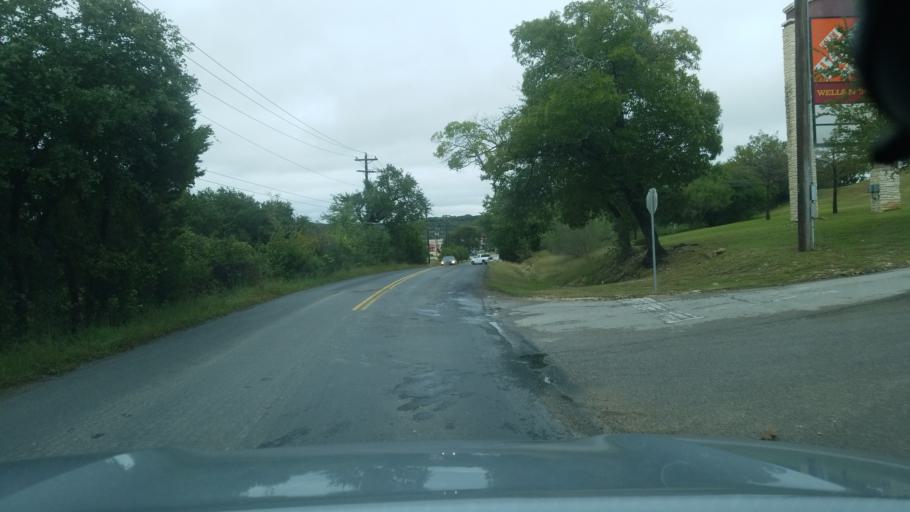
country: US
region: Texas
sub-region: Comal County
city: Bulverde
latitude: 29.7968
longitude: -98.4244
